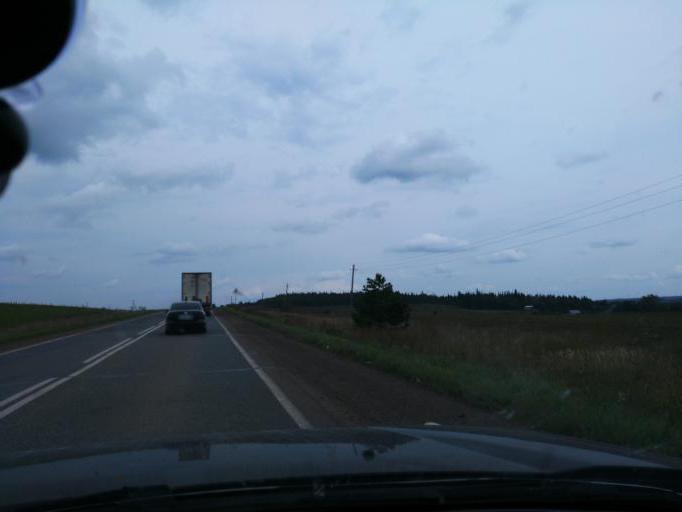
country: RU
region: Perm
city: Kuyeda
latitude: 56.4630
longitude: 55.6602
